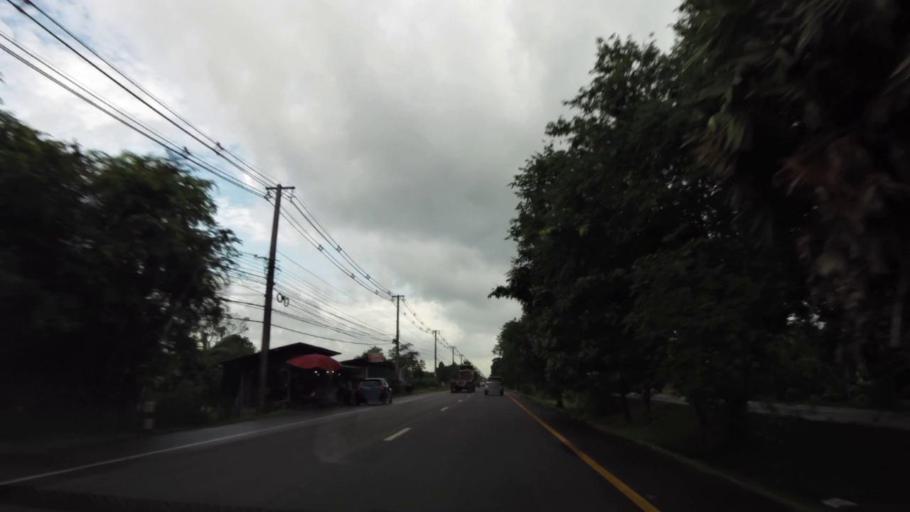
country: TH
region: Chanthaburi
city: Khlung
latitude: 12.4722
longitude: 102.1926
